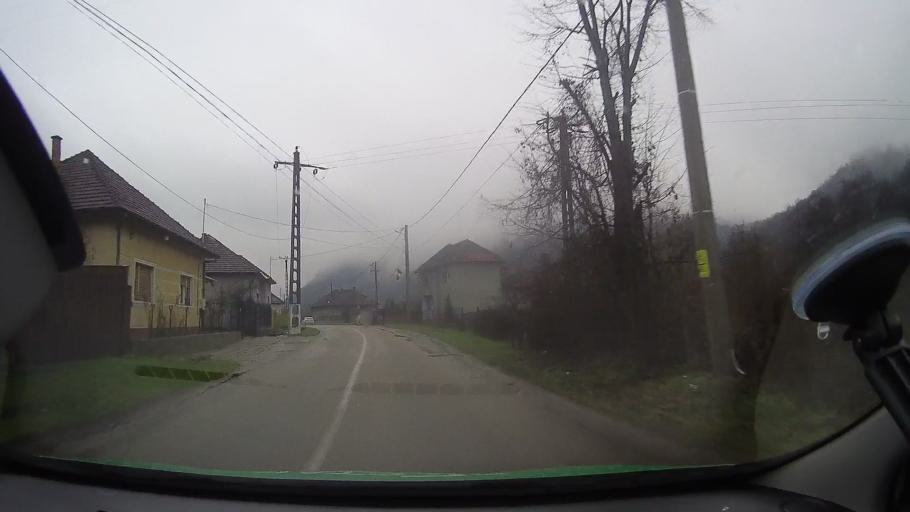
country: RO
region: Arad
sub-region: Comuna Moneasa
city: Moneasa
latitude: 46.4274
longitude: 22.2546
